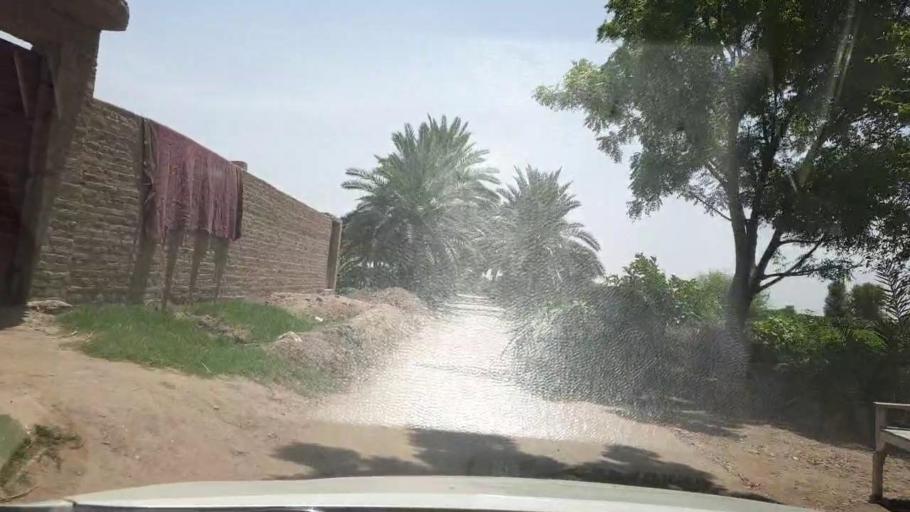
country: PK
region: Sindh
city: Bozdar
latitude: 27.2049
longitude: 68.6692
